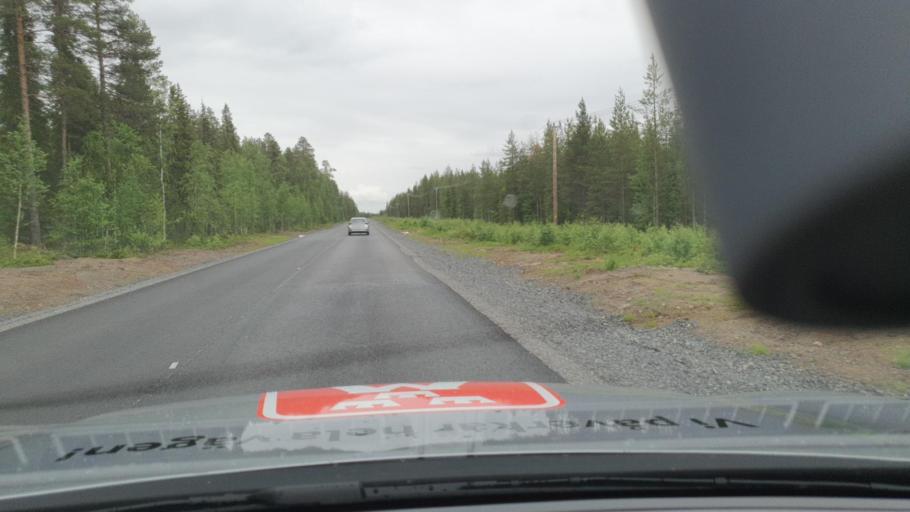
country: SE
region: Norrbotten
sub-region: Overkalix Kommun
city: OEverkalix
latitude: 66.6830
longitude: 23.2137
